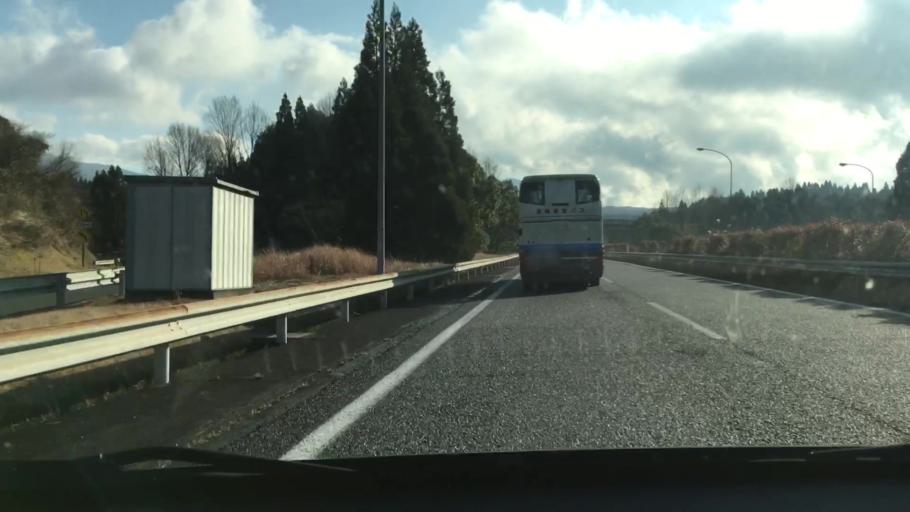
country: JP
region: Kagoshima
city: Okuchi-shinohara
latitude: 32.0353
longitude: 130.7991
